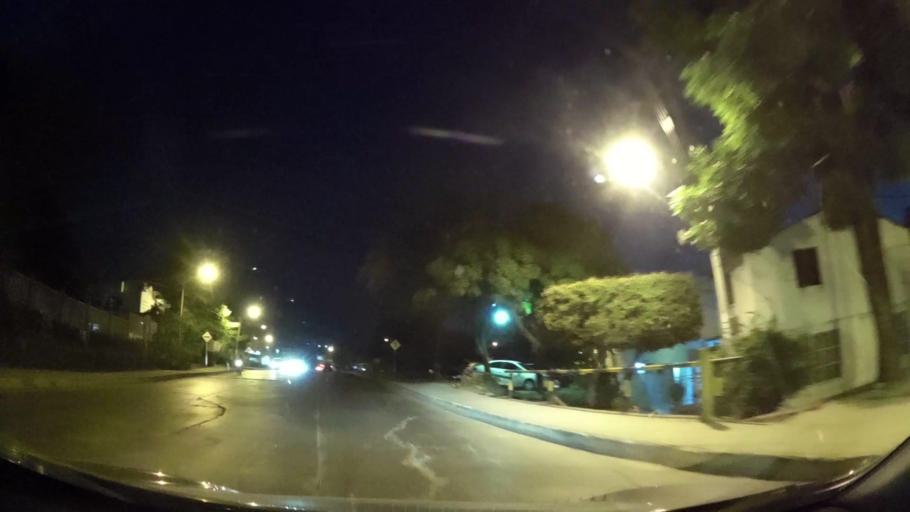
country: CO
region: Bolivar
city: Cartagena
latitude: 10.3853
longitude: -75.4945
